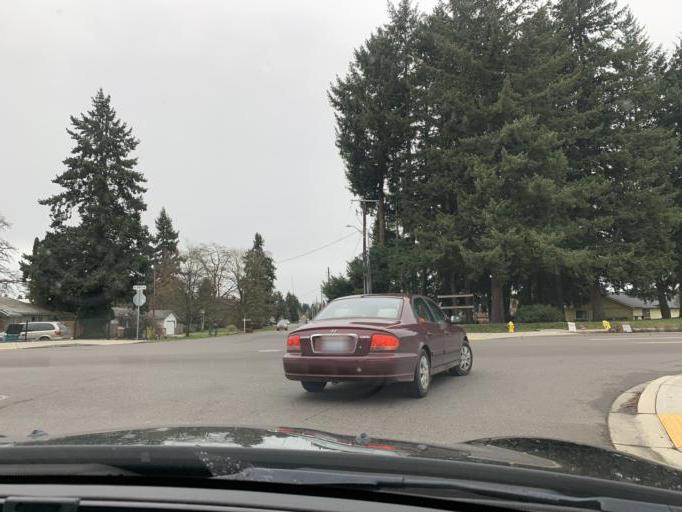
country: US
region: Washington
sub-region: Clark County
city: Five Corners
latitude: 45.6844
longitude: -122.5765
